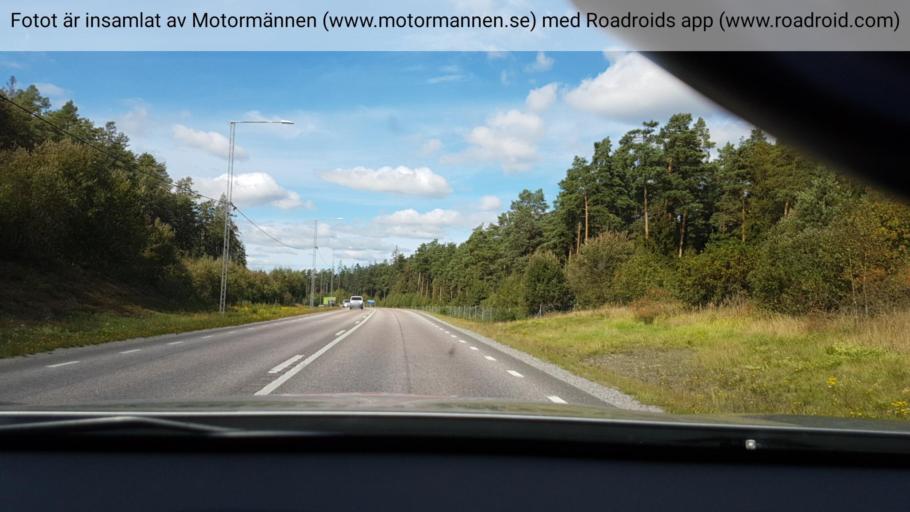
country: SE
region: Stockholm
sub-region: Vallentuna Kommun
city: Vallentuna
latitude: 59.4930
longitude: 18.1076
